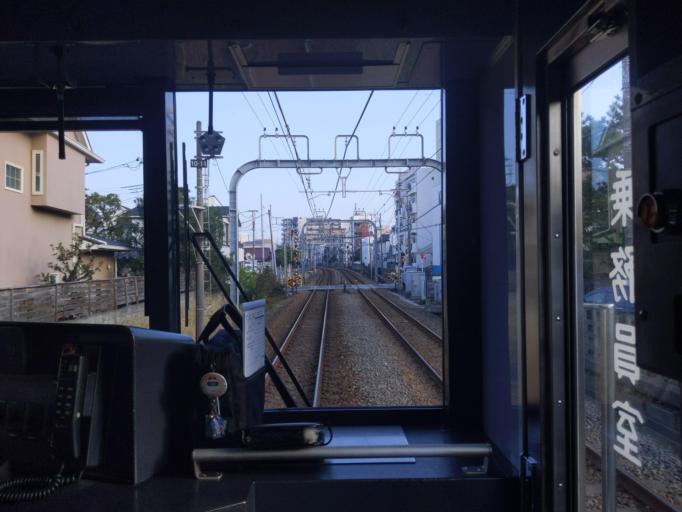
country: JP
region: Kanagawa
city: Fujisawa
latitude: 35.3126
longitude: 139.4795
